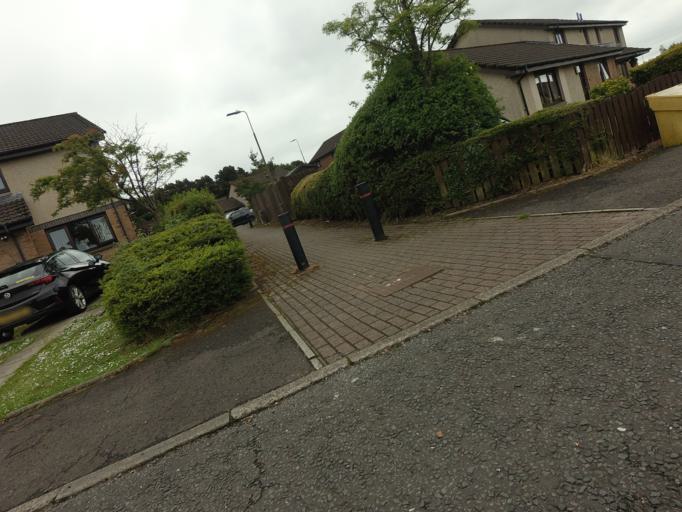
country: GB
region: Scotland
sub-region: West Lothian
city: Livingston
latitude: 55.9004
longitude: -3.5277
